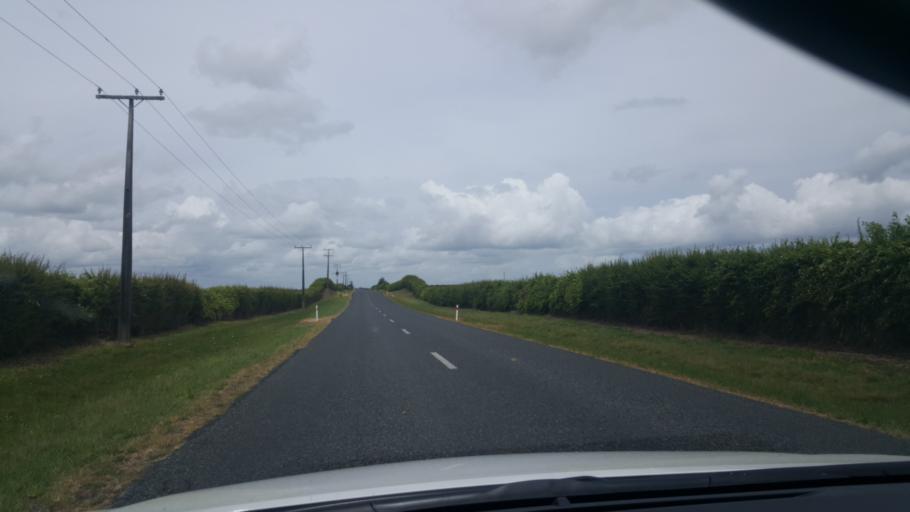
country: NZ
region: Waikato
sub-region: Matamata-Piako District
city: Matamata
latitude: -37.8768
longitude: 175.7274
